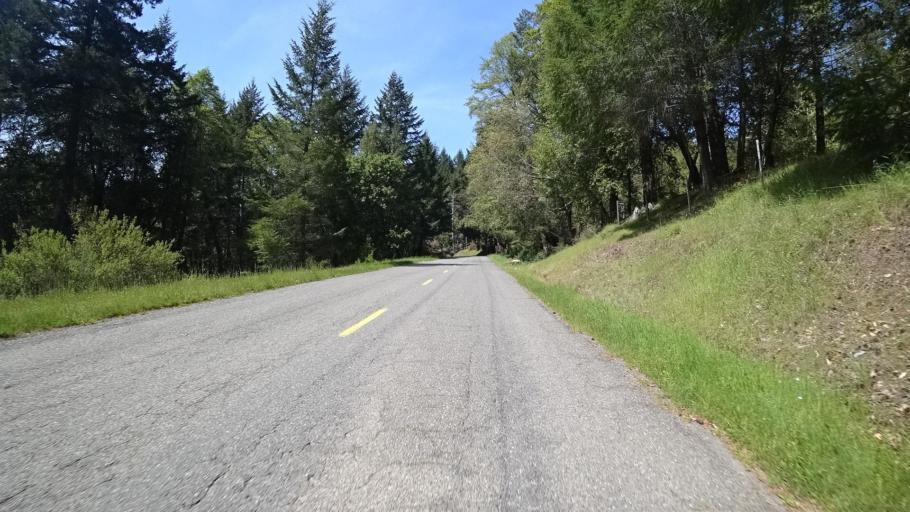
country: US
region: California
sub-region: Humboldt County
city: Redway
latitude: 40.3495
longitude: -123.7144
